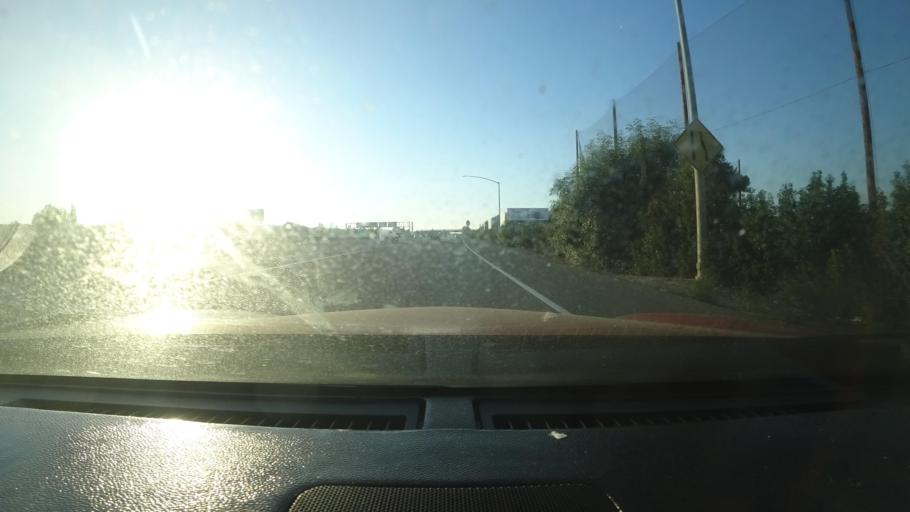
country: US
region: California
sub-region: Santa Clara County
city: Alum Rock
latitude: 37.3429
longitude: -121.8547
